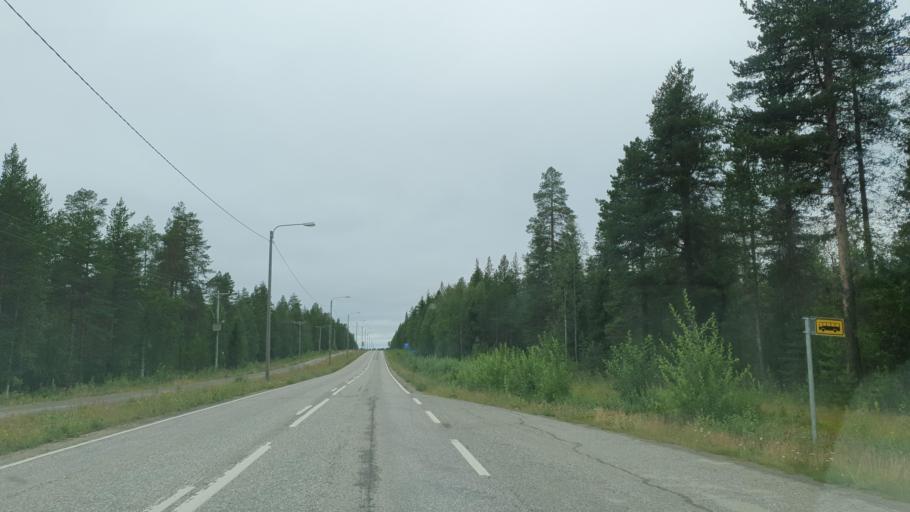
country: FI
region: Lapland
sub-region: Pohjois-Lappi
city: Sodankylae
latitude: 67.4085
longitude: 26.6376
